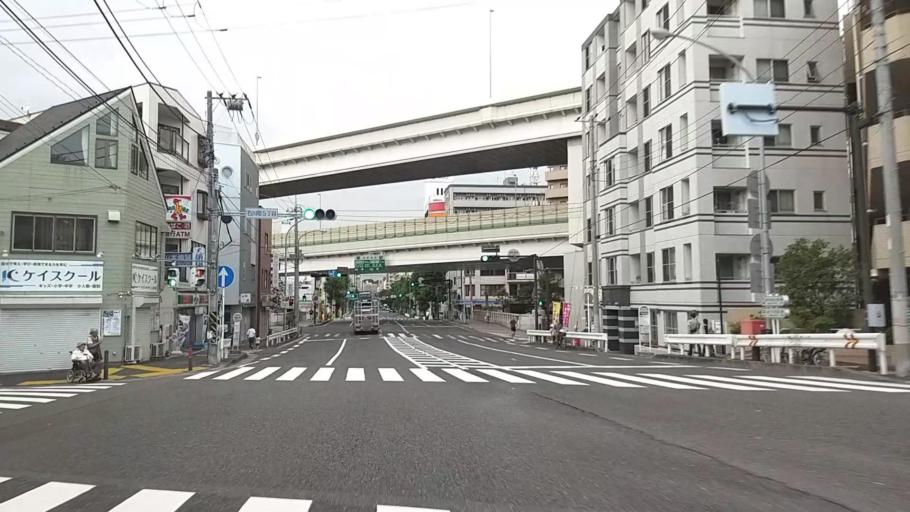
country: JP
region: Kanagawa
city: Yokohama
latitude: 35.4366
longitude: 139.6379
